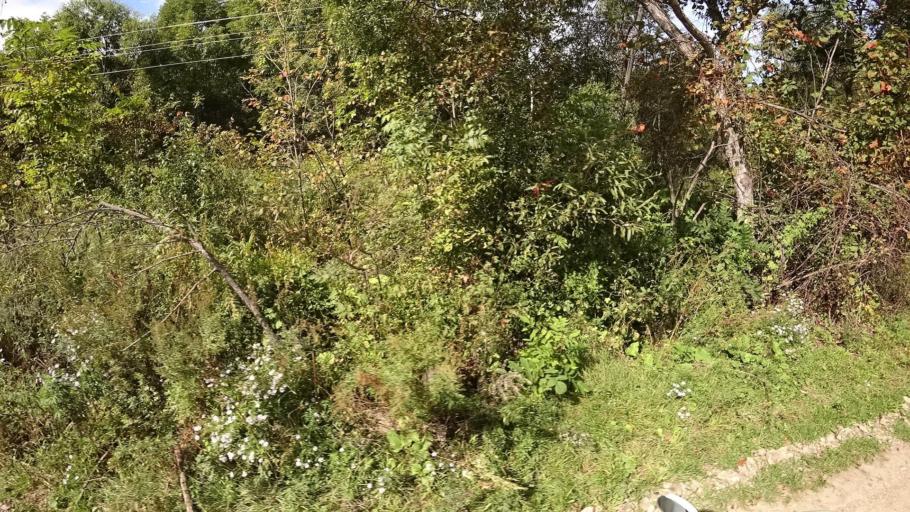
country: RU
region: Primorskiy
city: Kirovskiy
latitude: 44.7567
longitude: 133.6113
